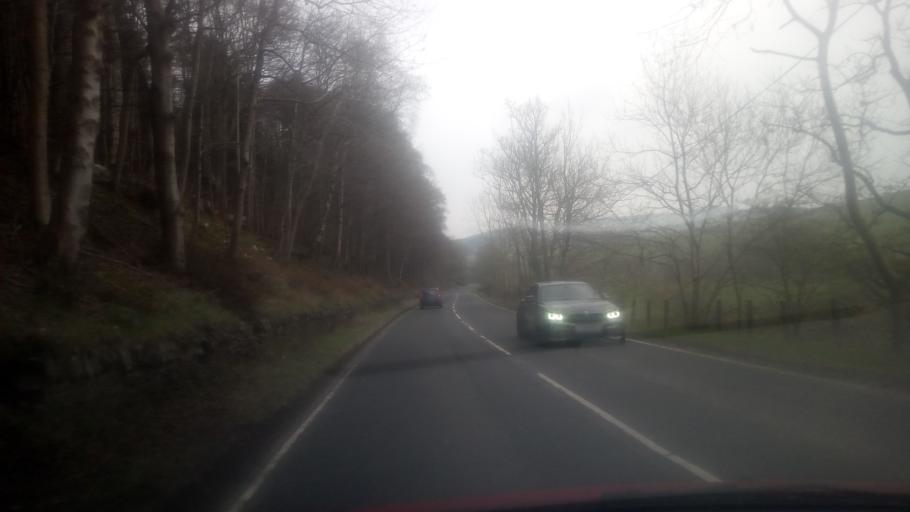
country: GB
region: Scotland
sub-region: The Scottish Borders
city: Galashiels
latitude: 55.6865
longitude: -2.8644
